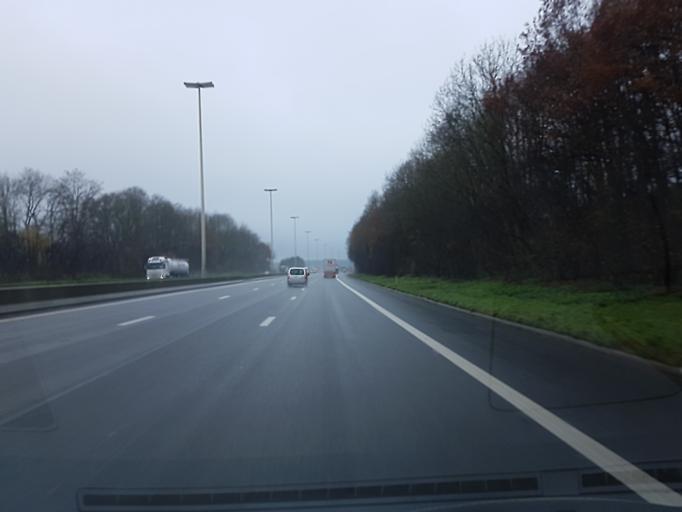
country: BE
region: Wallonia
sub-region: Province de Liege
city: Heron
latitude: 50.5352
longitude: 5.1152
